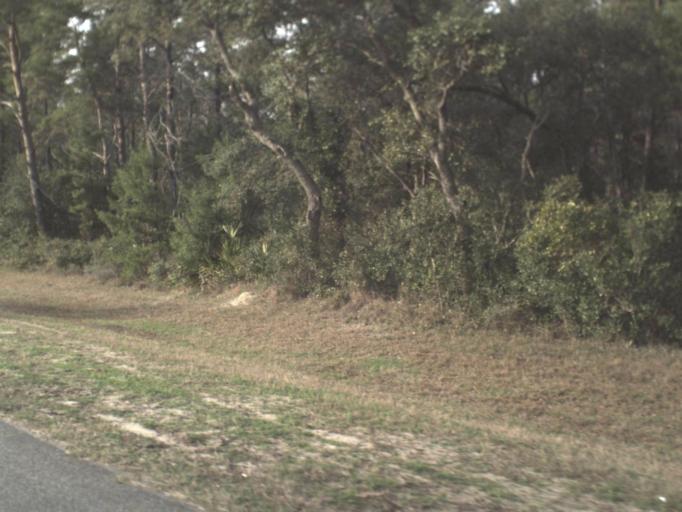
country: US
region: Florida
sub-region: Bay County
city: Mexico Beach
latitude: 29.9649
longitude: -85.4469
